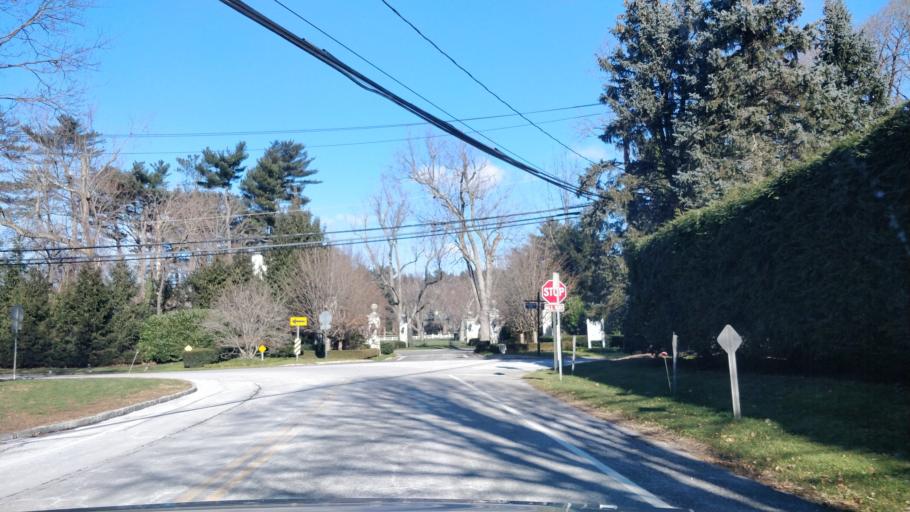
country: US
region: New York
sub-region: Nassau County
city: East Hills
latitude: 40.7910
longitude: -73.6147
